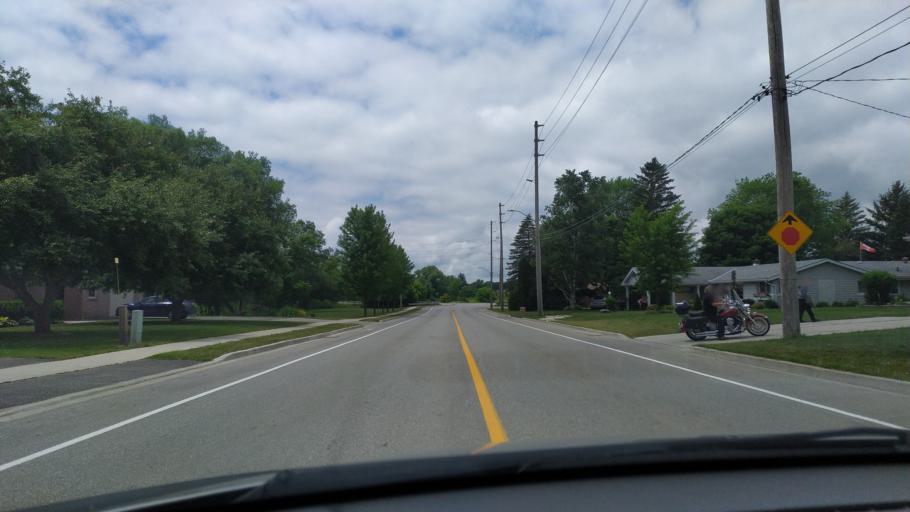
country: CA
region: Ontario
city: Stratford
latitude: 43.3893
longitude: -80.9655
